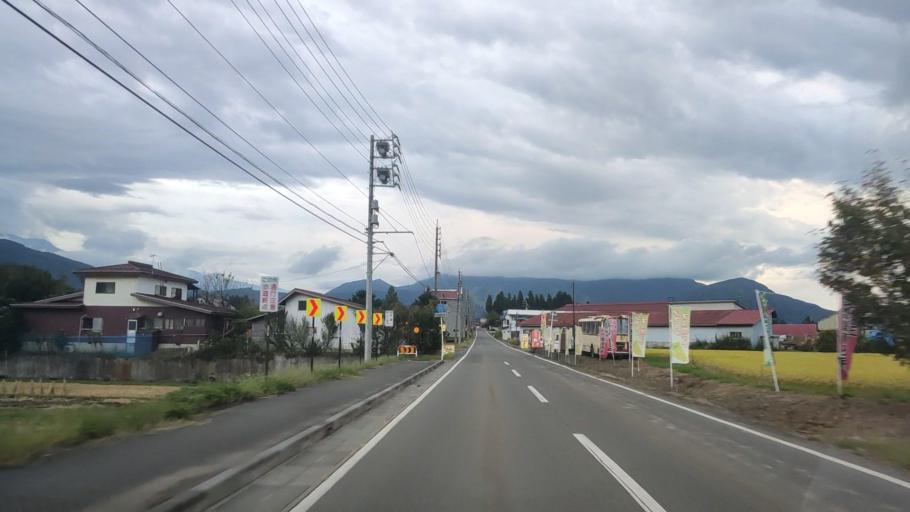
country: JP
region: Nagano
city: Iiyama
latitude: 36.8727
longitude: 138.4077
